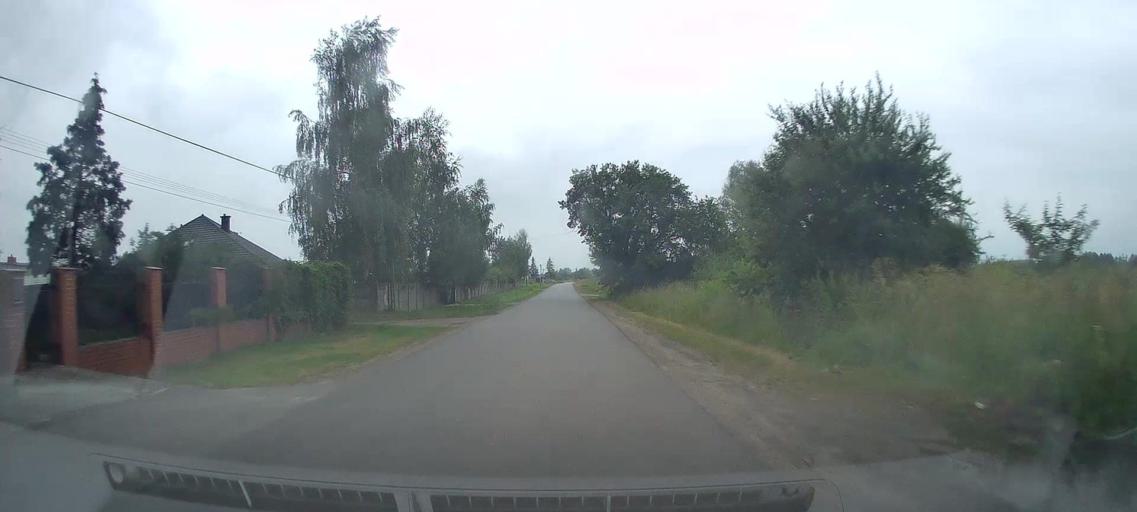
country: PL
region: Masovian Voivodeship
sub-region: Powiat radomski
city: Jedlinsk
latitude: 51.4705
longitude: 21.1098
